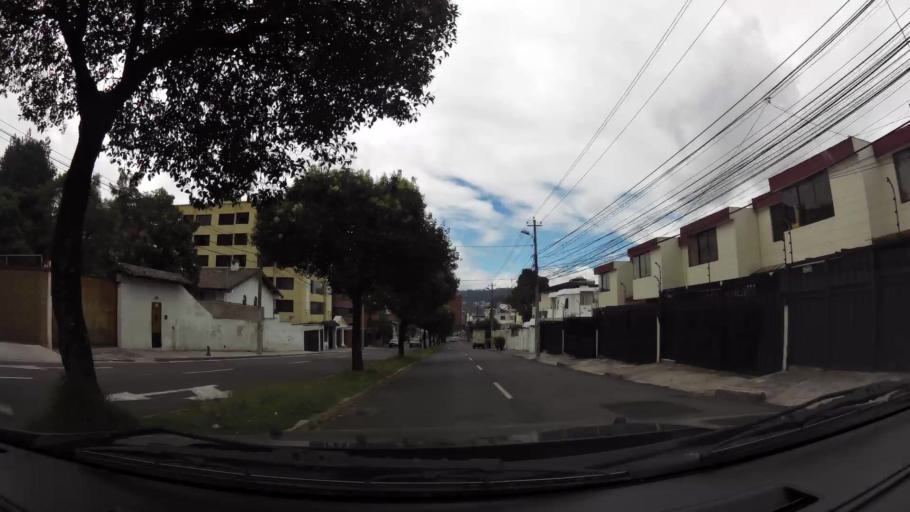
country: EC
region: Pichincha
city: Quito
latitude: -0.1706
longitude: -78.4923
